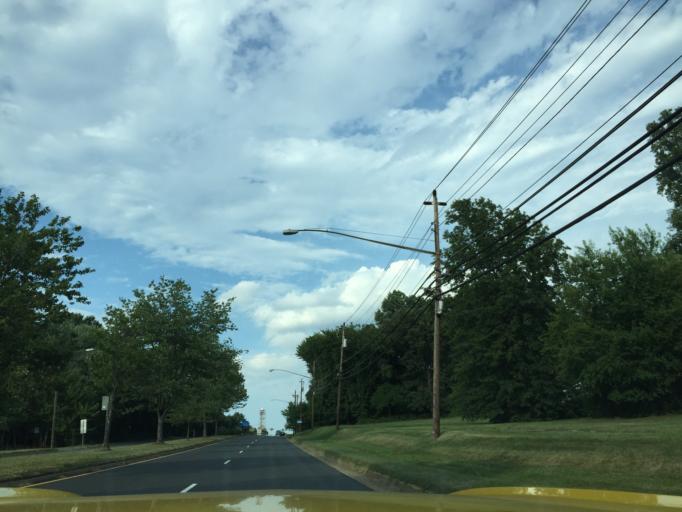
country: US
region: Virginia
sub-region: Fairfax County
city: Tysons Corner
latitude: 38.9143
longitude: -77.2424
